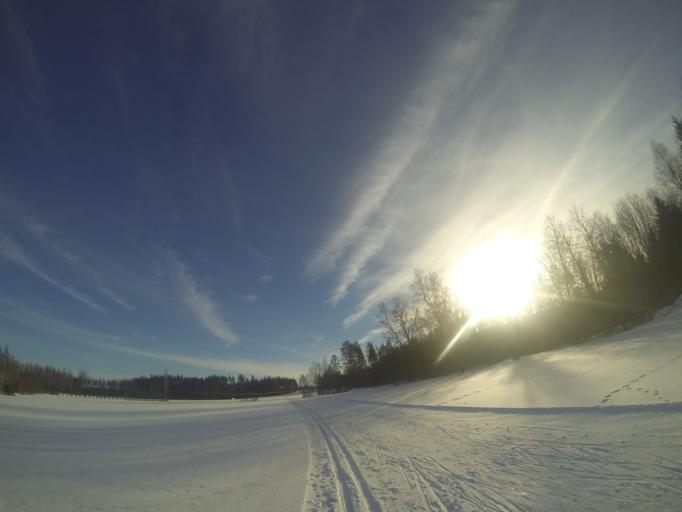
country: FI
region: Southern Savonia
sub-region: Savonlinna
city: Savonlinna
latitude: 61.9417
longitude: 28.9182
